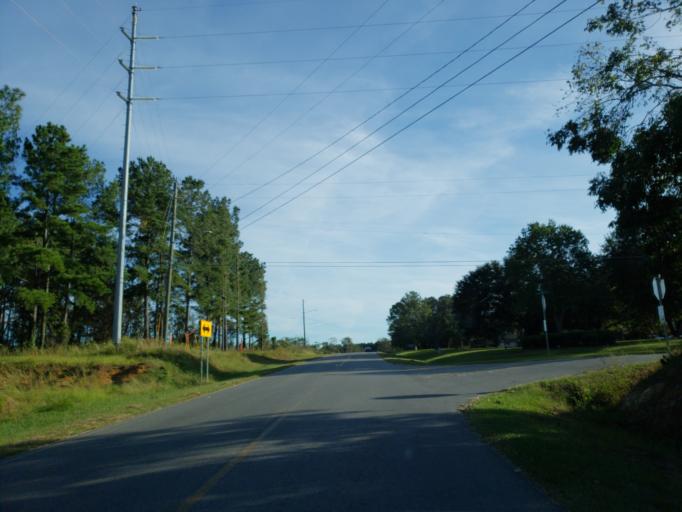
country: US
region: Georgia
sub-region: Dooly County
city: Vienna
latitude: 32.0833
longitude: -83.7878
